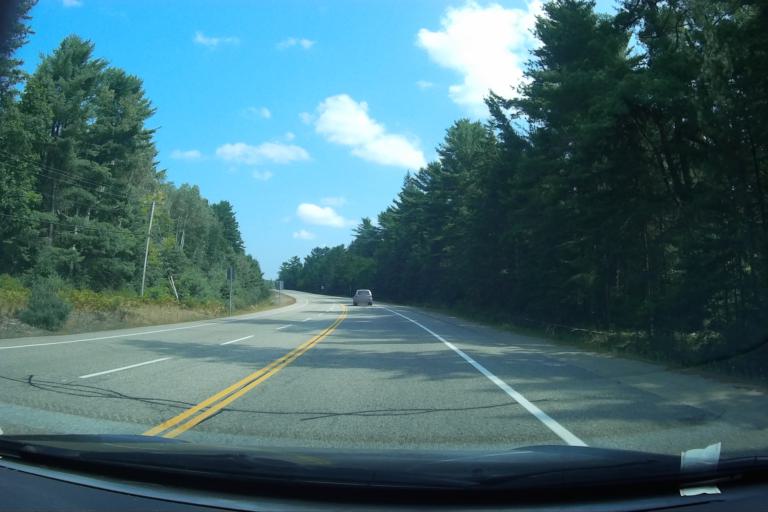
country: CA
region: Ontario
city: Huntsville
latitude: 45.5802
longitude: -78.5020
